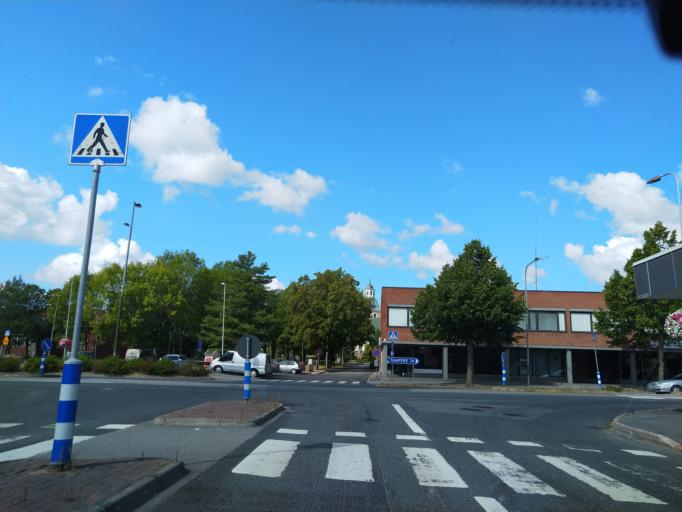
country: FI
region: Satakunta
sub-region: Pori
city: Huittinen
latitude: 61.1799
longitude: 22.6974
